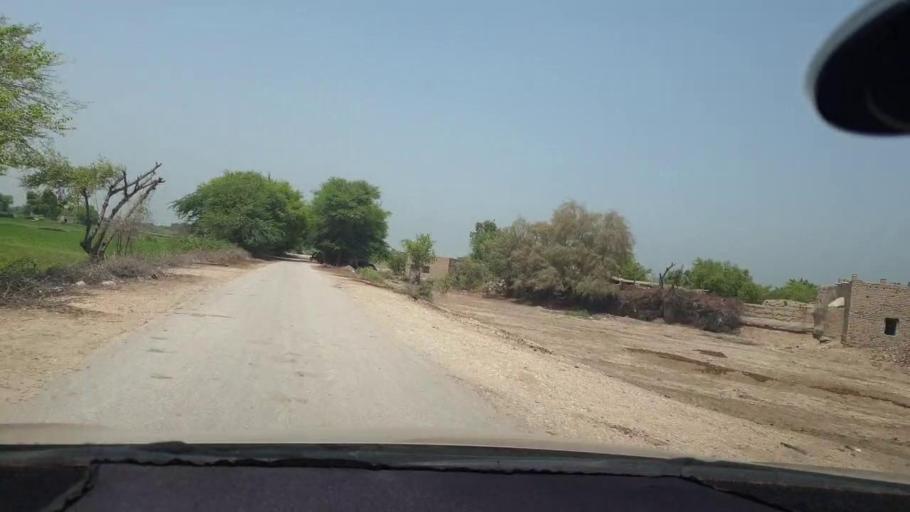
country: PK
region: Sindh
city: Kambar
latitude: 27.6668
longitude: 67.9145
